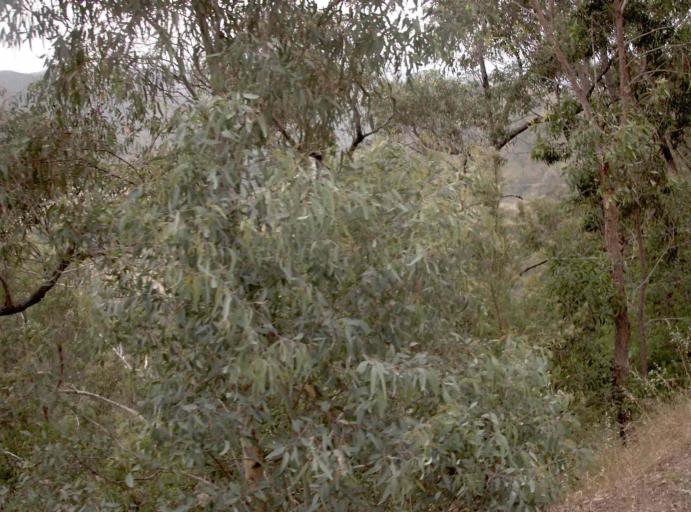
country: AU
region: Victoria
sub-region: Wellington
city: Heyfield
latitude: -37.7081
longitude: 146.6676
